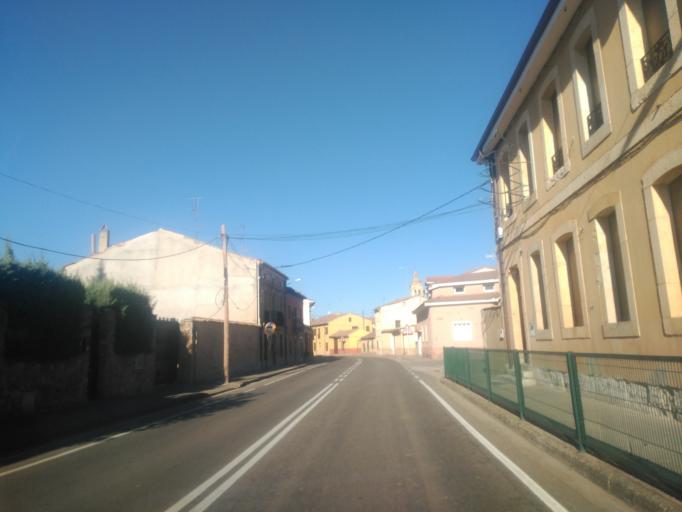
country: ES
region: Castille and Leon
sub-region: Provincia de Burgos
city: Zazuar
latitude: 41.6948
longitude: -3.5519
